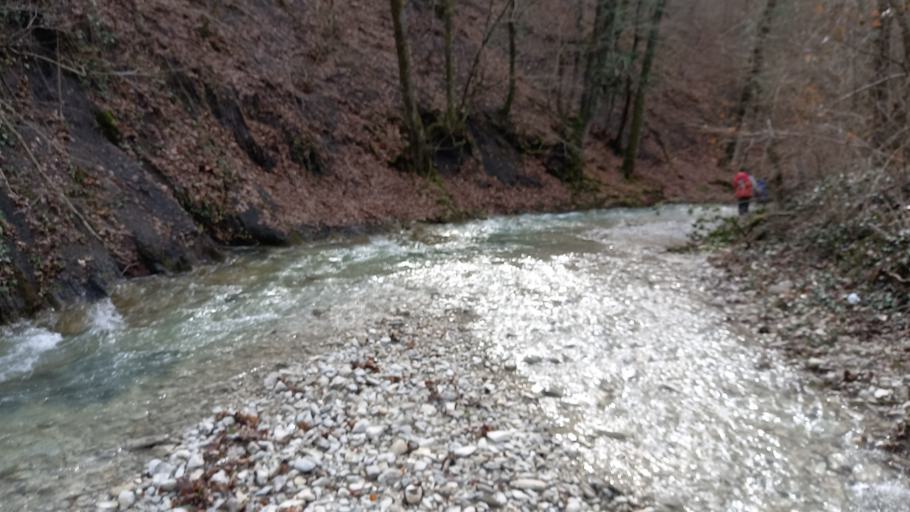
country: RU
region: Krasnodarskiy
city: Dzhubga
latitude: 44.4080
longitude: 38.7151
